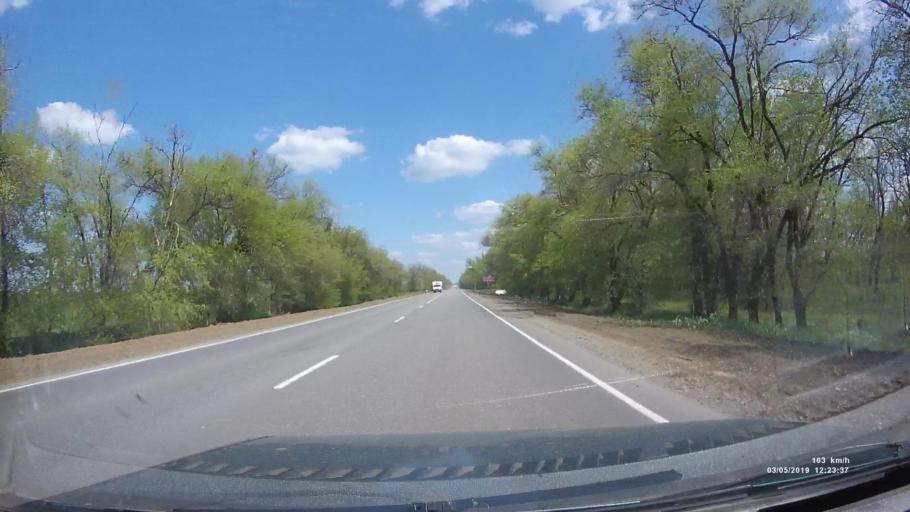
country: RU
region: Rostov
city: Semikarakorsk
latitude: 47.4109
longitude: 40.6861
